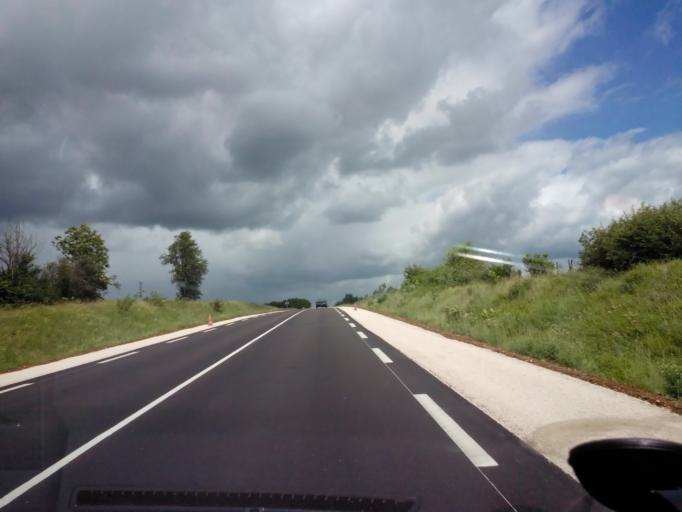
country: FR
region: Champagne-Ardenne
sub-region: Departement de la Haute-Marne
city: Rolampont
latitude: 47.9291
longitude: 5.2897
